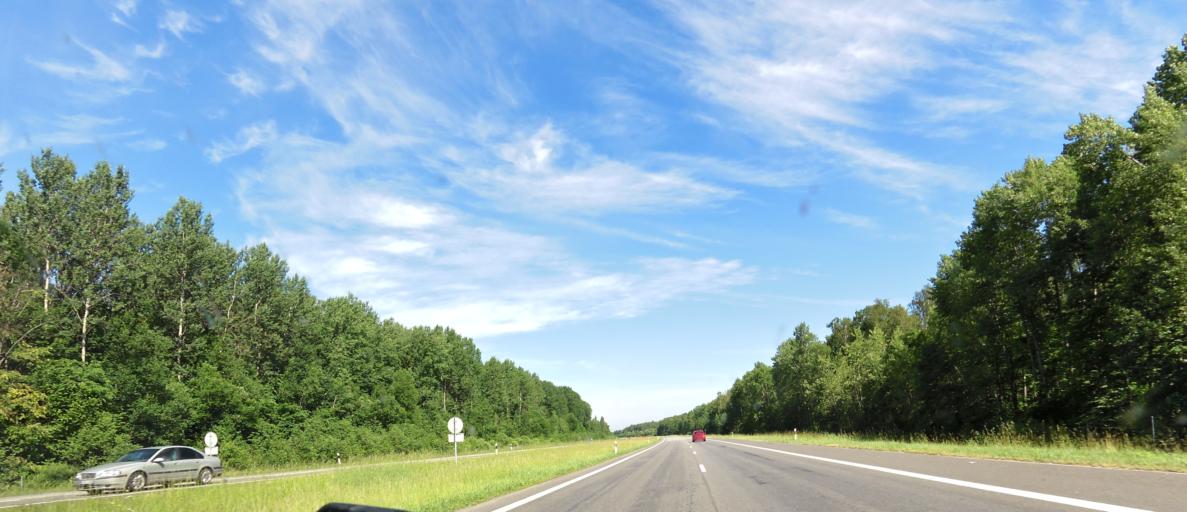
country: LT
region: Vilnius County
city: Ukmerge
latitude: 55.4571
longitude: 24.6668
